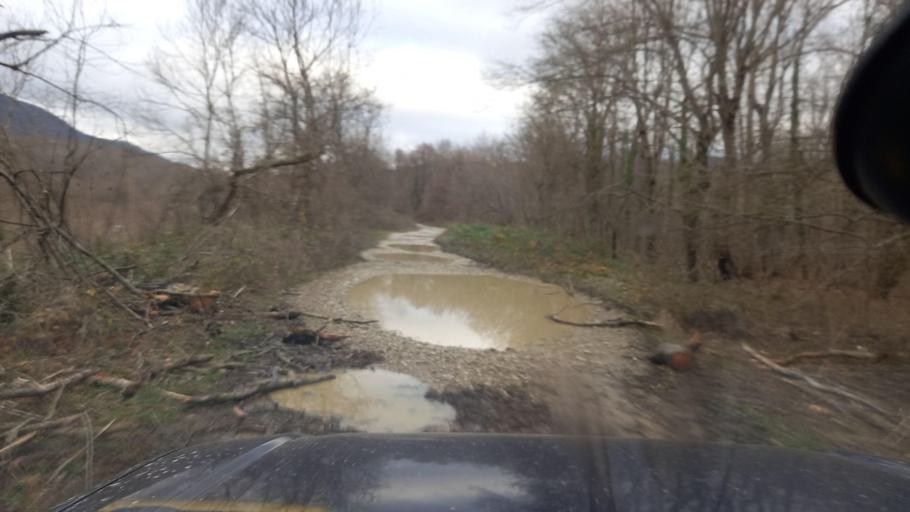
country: RU
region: Krasnodarskiy
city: Pshada
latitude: 44.4890
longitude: 38.4100
